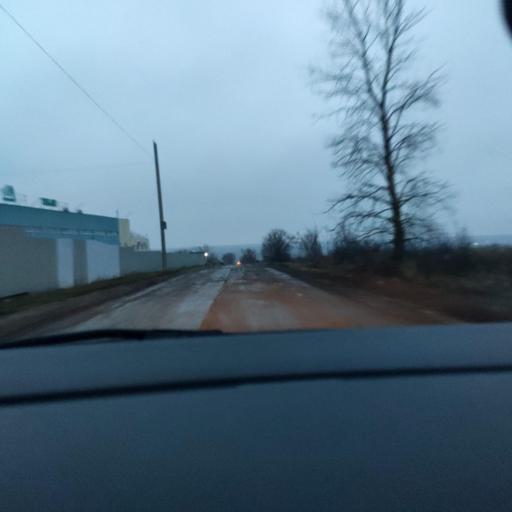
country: RU
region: Voronezj
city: Shilovo
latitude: 51.5724
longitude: 39.1351
